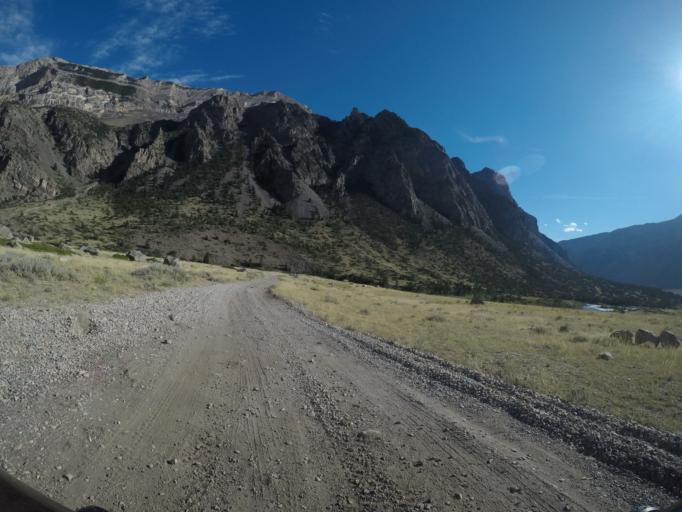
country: US
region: Montana
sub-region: Carbon County
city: Red Lodge
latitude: 44.8439
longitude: -109.3169
